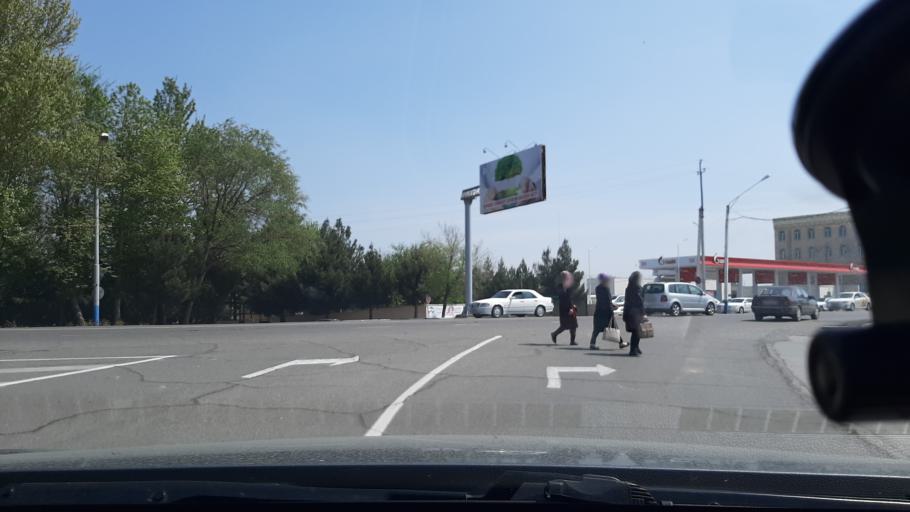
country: TJ
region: Viloyati Sughd
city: Khujand
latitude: 40.2921
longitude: 69.6400
